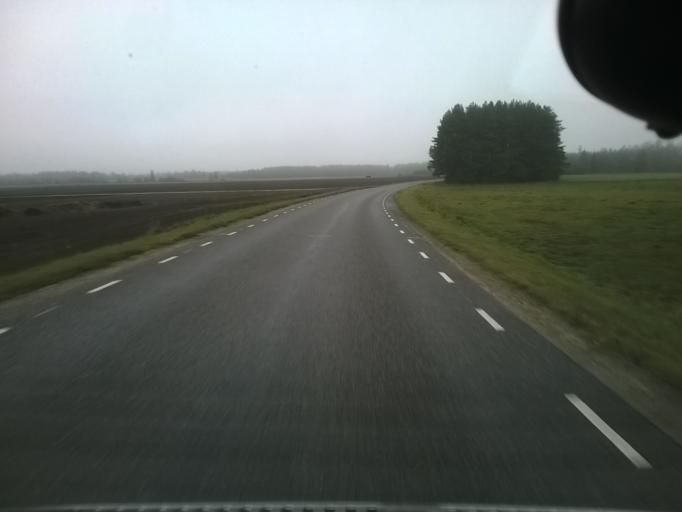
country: EE
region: Raplamaa
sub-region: Kohila vald
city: Kohila
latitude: 59.1800
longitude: 24.6561
